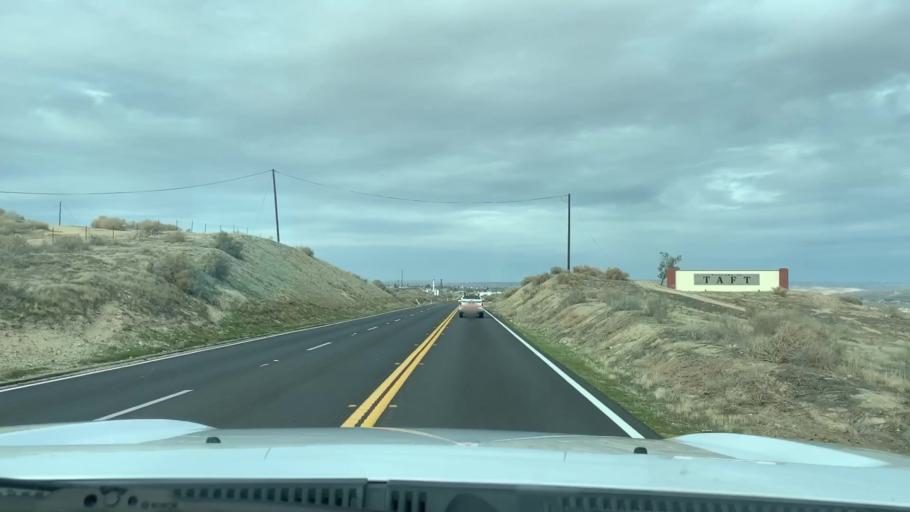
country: US
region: California
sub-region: Kern County
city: South Taft
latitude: 35.1234
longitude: -119.4376
